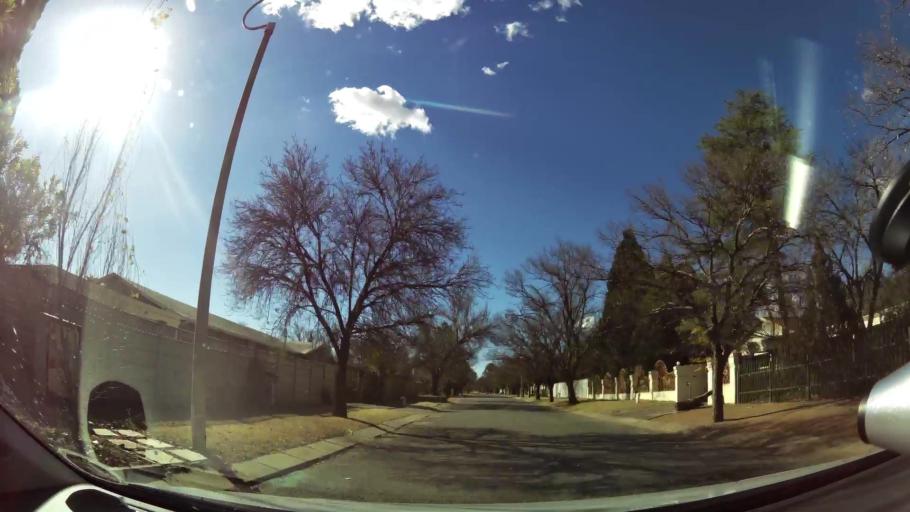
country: ZA
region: North-West
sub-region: Dr Kenneth Kaunda District Municipality
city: Klerksdorp
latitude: -26.8386
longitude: 26.6530
